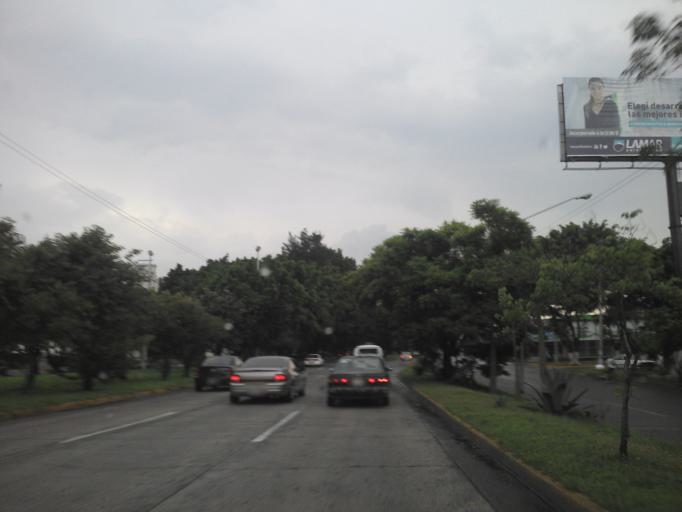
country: MX
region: Jalisco
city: Guadalajara
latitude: 20.6432
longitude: -103.3535
